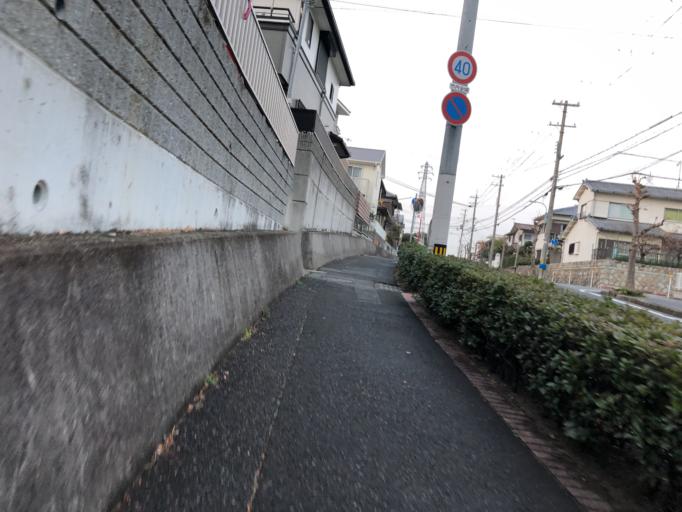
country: JP
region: Hyogo
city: Akashi
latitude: 34.6495
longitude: 135.0184
